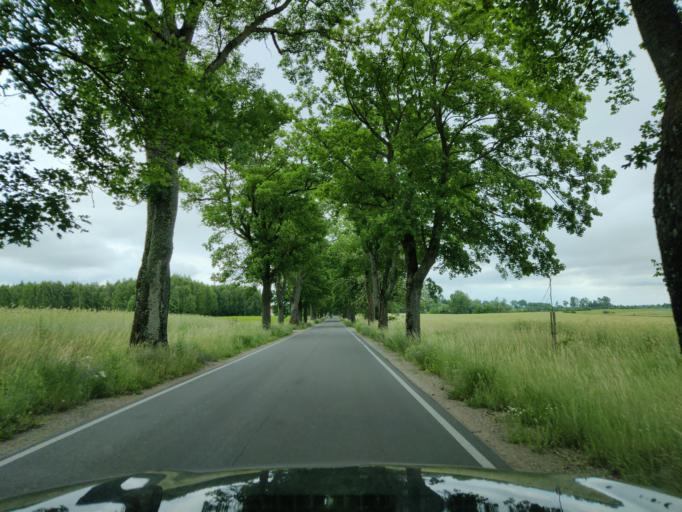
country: PL
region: Warmian-Masurian Voivodeship
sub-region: Powiat mragowski
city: Mikolajki
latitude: 53.8570
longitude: 21.6102
